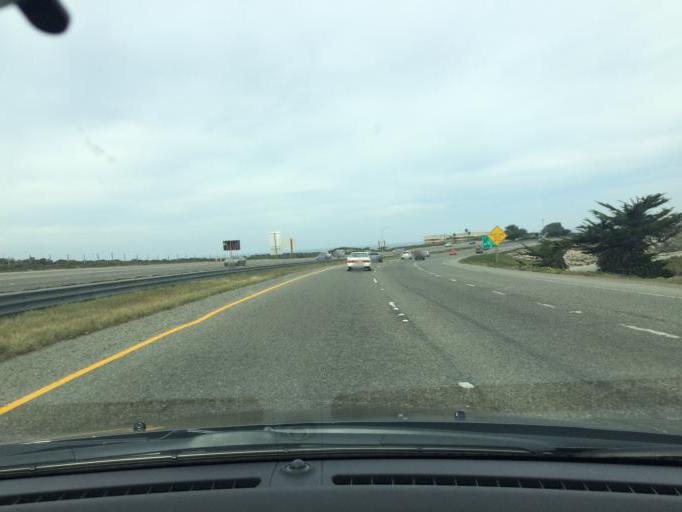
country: US
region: California
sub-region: Monterey County
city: Seaside
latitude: 36.6060
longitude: -121.8609
